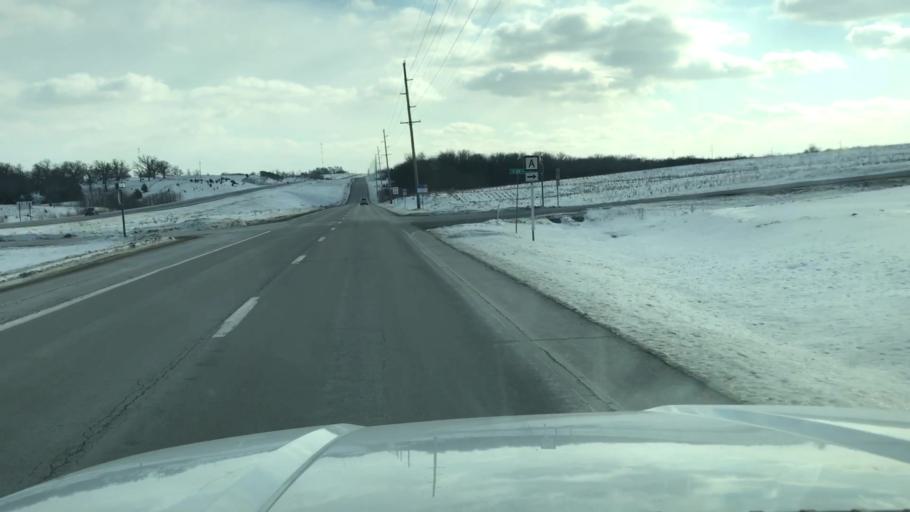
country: US
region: Missouri
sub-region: Nodaway County
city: Maryville
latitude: 40.2008
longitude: -94.8682
